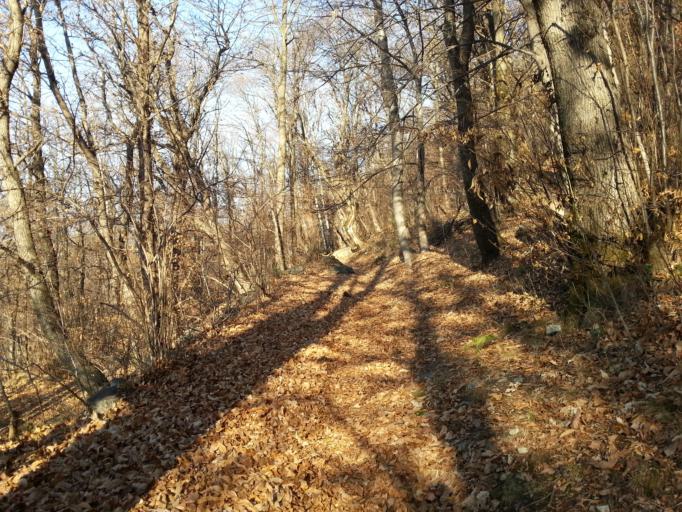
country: CH
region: Ticino
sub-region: Bellinzona District
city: Cadenazzo
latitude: 46.1275
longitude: 8.9259
